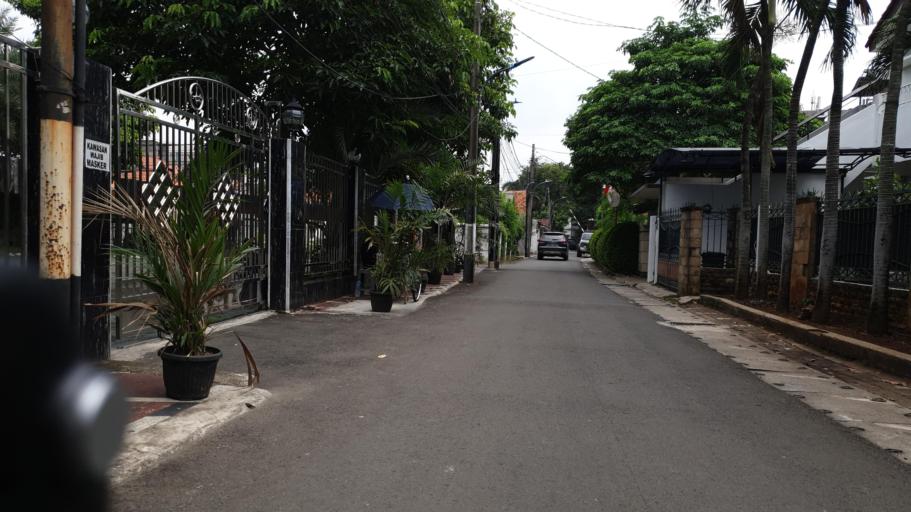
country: ID
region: Jakarta Raya
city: Jakarta
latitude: -6.2745
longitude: 106.7962
